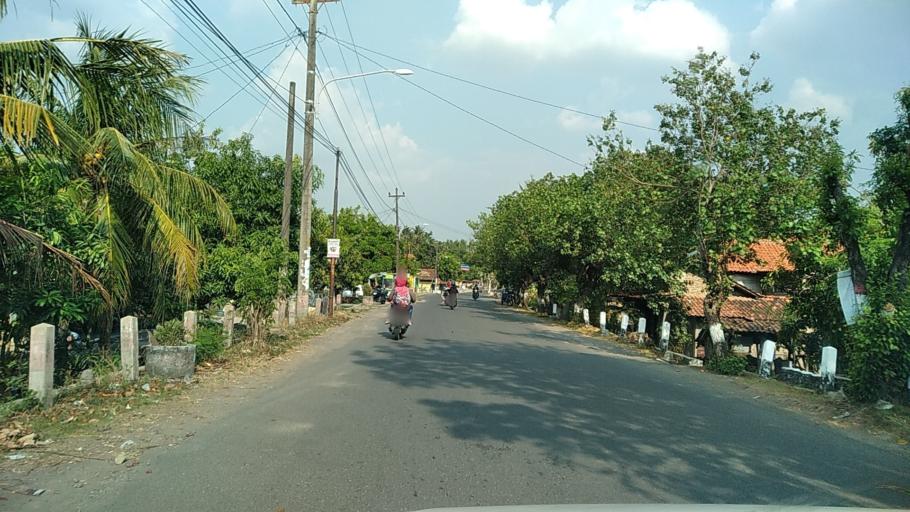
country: ID
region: Central Java
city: Mranggen
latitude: -6.9748
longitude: 110.4978
